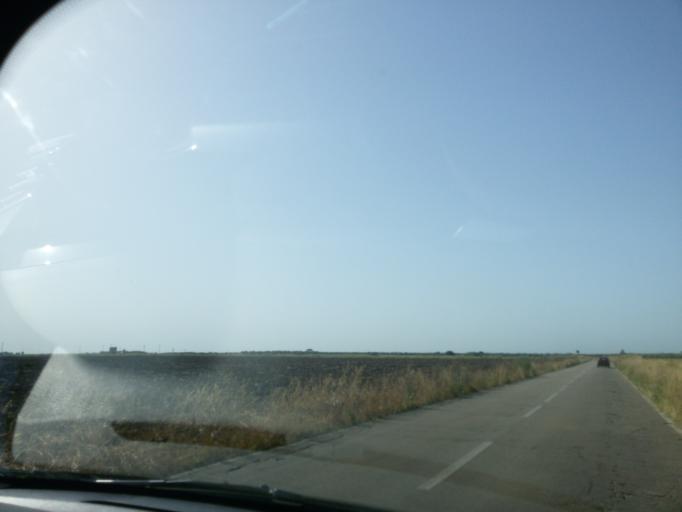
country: IT
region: Apulia
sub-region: Provincia di Brindisi
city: Mesagne
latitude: 40.5295
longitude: 17.8197
